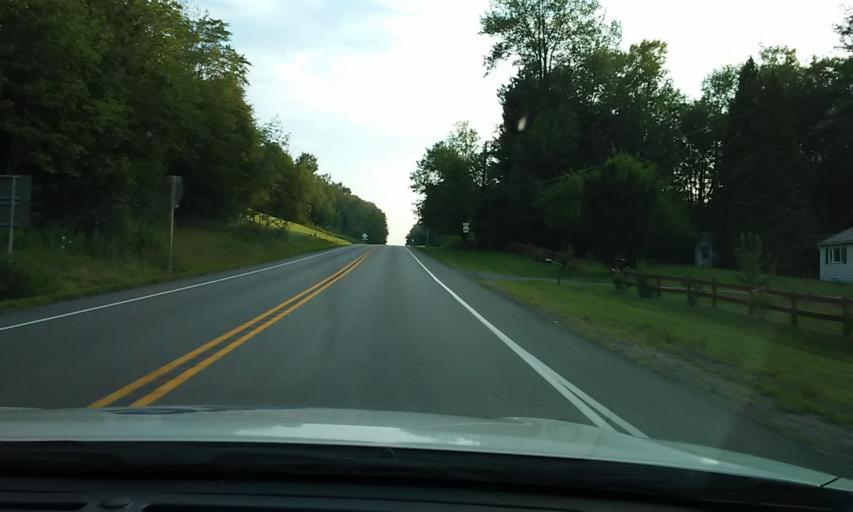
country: US
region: Pennsylvania
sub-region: Forest County
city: Marienville
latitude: 41.5293
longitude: -79.0516
